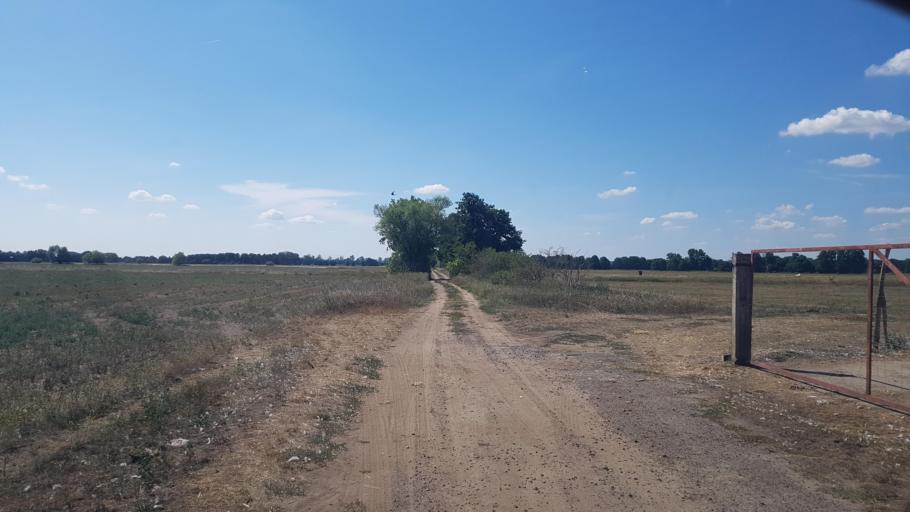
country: DE
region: Brandenburg
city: Golzow
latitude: 52.2449
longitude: 12.6602
